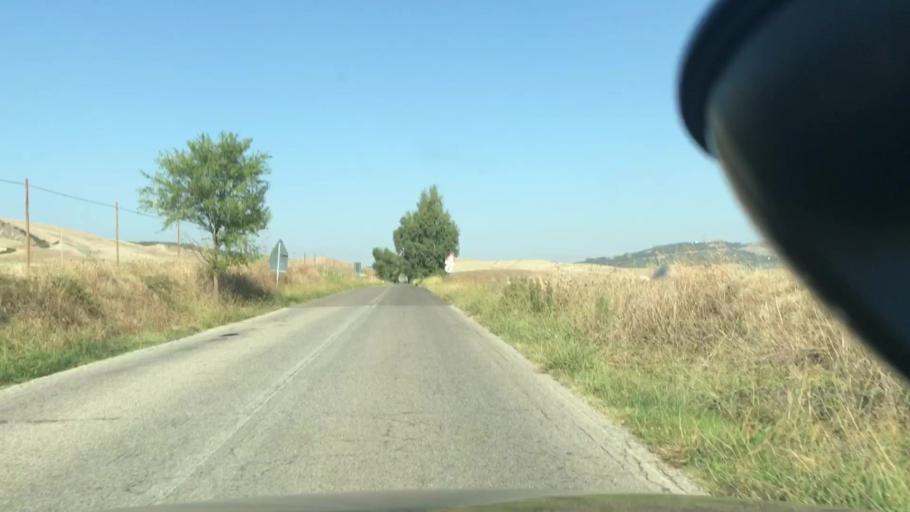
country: IT
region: Basilicate
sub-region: Provincia di Matera
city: La Martella
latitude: 40.6586
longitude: 16.5166
